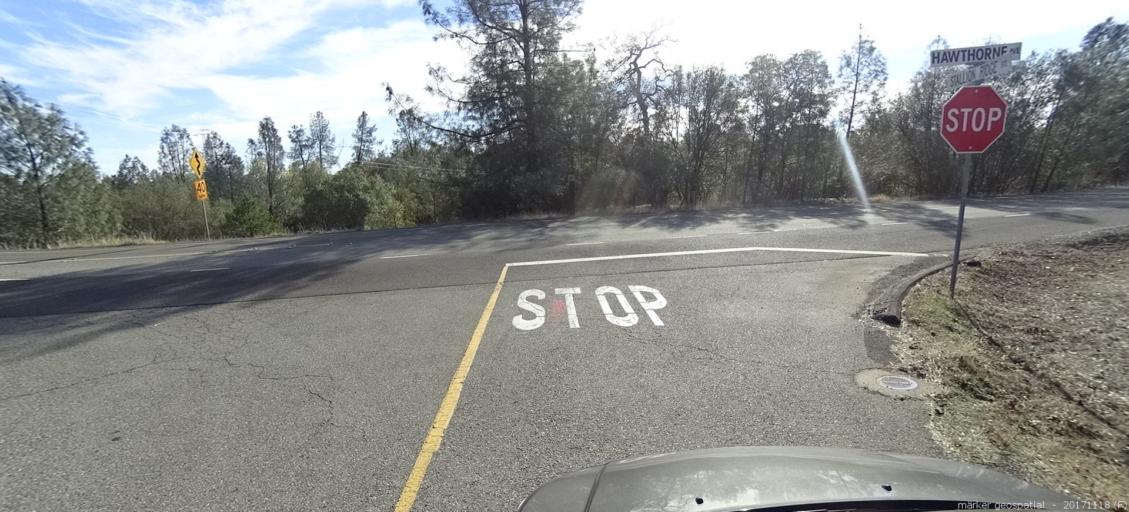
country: US
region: California
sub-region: Shasta County
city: Redding
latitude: 40.4788
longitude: -122.4287
